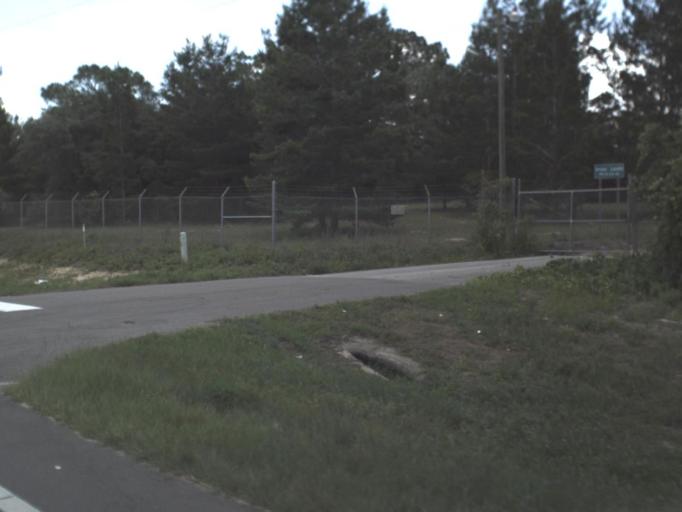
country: US
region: Florida
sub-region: Alachua County
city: Archer
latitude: 29.5187
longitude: -82.5460
